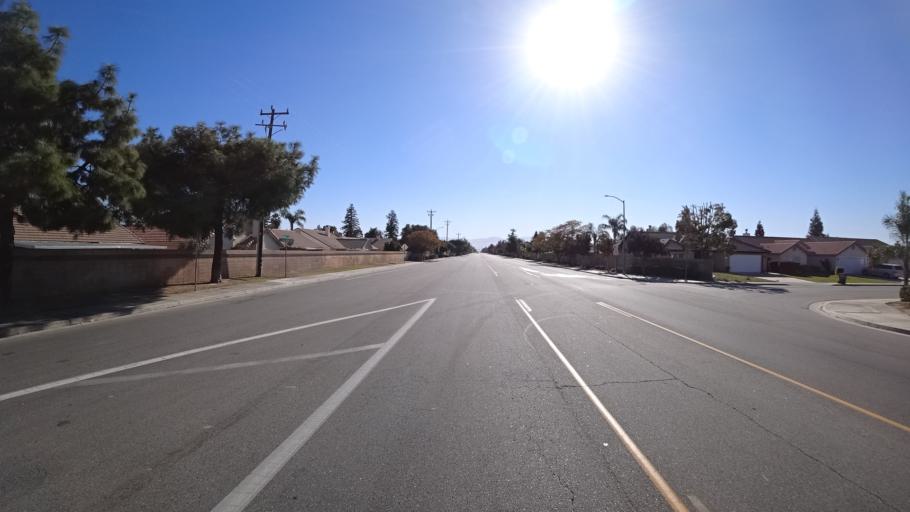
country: US
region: California
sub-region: Kern County
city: Greenfield
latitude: 35.2880
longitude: -119.0478
